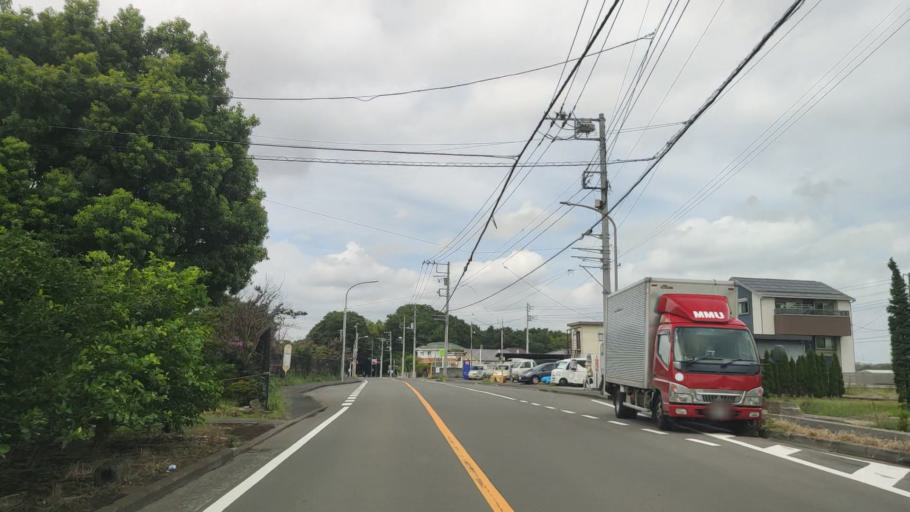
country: JP
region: Kanagawa
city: Minami-rinkan
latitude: 35.4819
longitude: 139.4752
